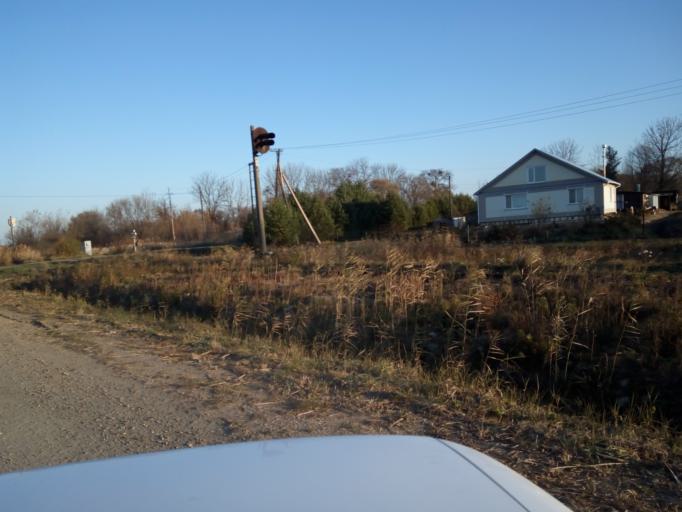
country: RU
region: Primorskiy
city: Lazo
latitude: 45.8651
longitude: 133.6435
